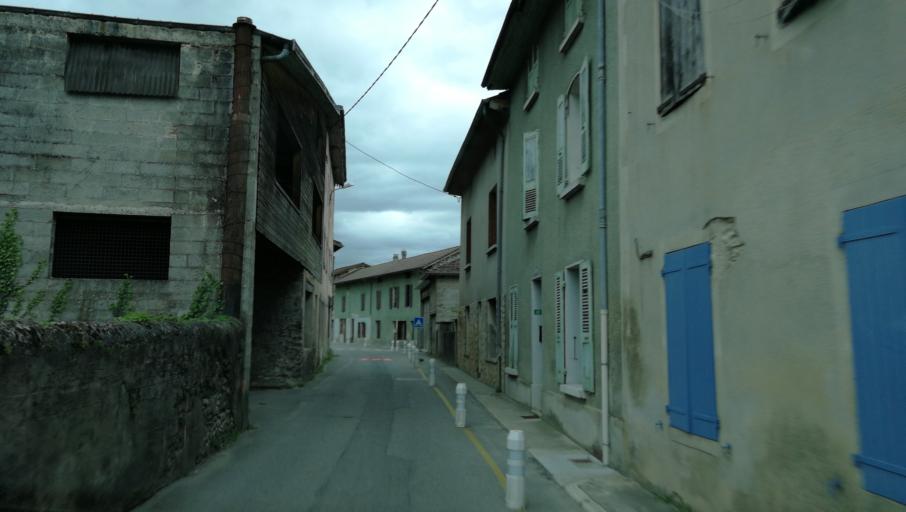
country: FR
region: Rhone-Alpes
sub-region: Departement de la Drome
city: Saint-Jean-en-Royans
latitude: 45.0158
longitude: 5.2885
